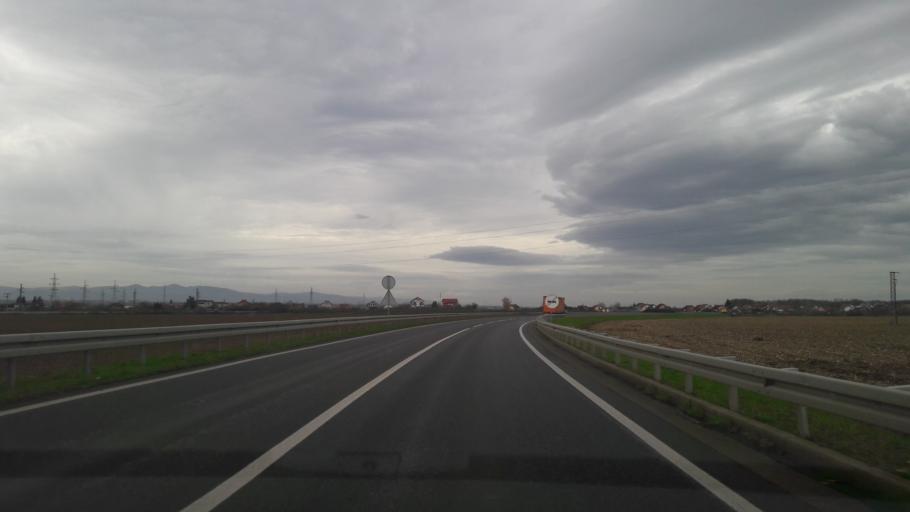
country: HR
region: Osjecko-Baranjska
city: Velimirovac
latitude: 45.5107
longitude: 18.1042
